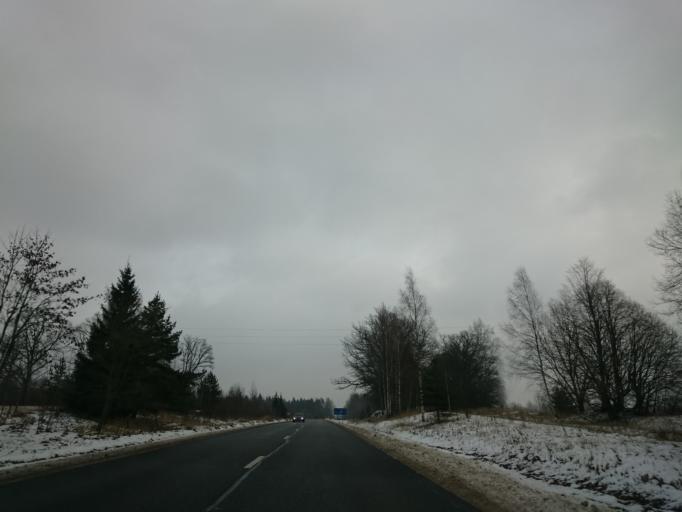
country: LV
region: Pargaujas
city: Stalbe
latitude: 57.3724
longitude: 25.0166
